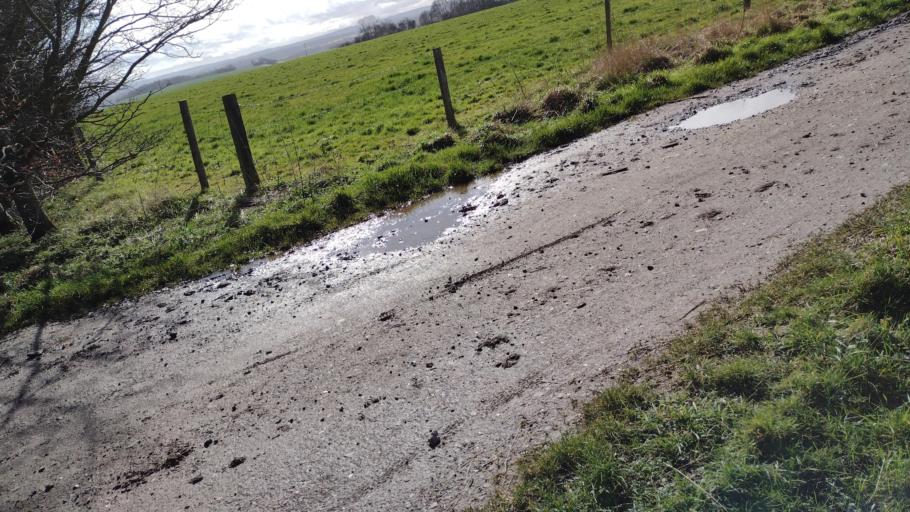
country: GB
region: England
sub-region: Wiltshire
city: Mildenhall
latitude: 51.4624
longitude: -1.6970
